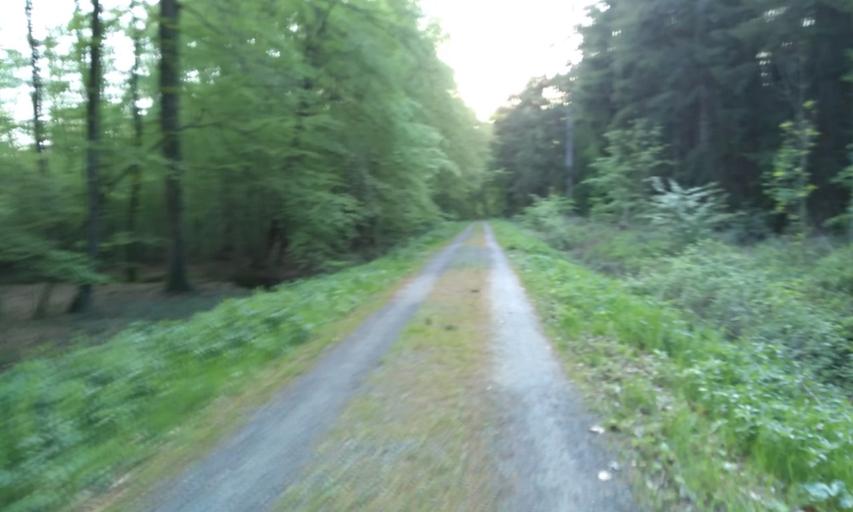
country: DE
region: Lower Saxony
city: Harsefeld
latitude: 53.4205
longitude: 9.4924
